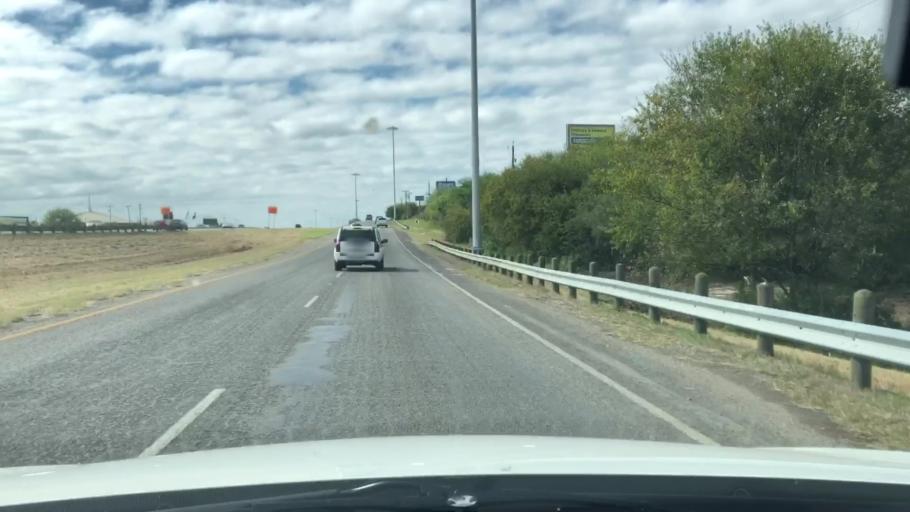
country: US
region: Texas
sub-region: Bexar County
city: Lackland Air Force Base
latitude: 29.4057
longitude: -98.6134
